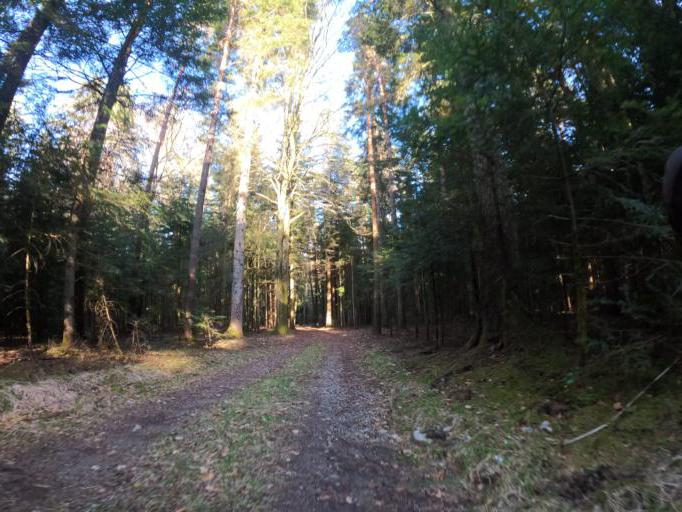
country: DE
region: Baden-Wuerttemberg
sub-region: Karlsruhe Region
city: Neuweiler
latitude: 48.7065
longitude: 8.6230
